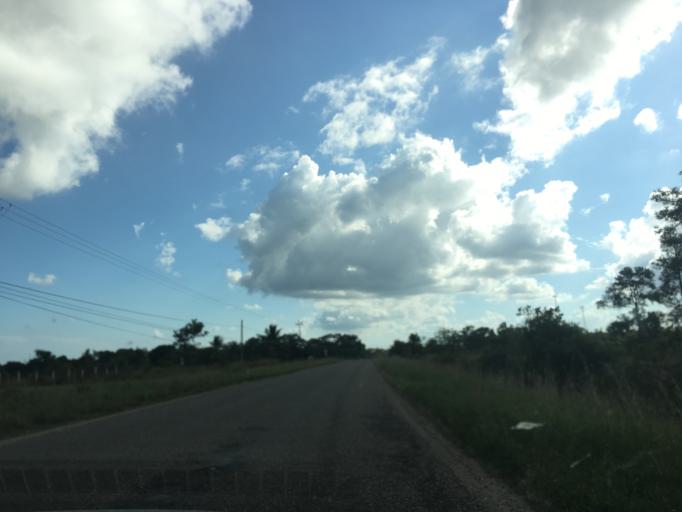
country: BZ
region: Stann Creek
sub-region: Dangriga
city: Dangriga
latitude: 16.8915
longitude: -88.3384
